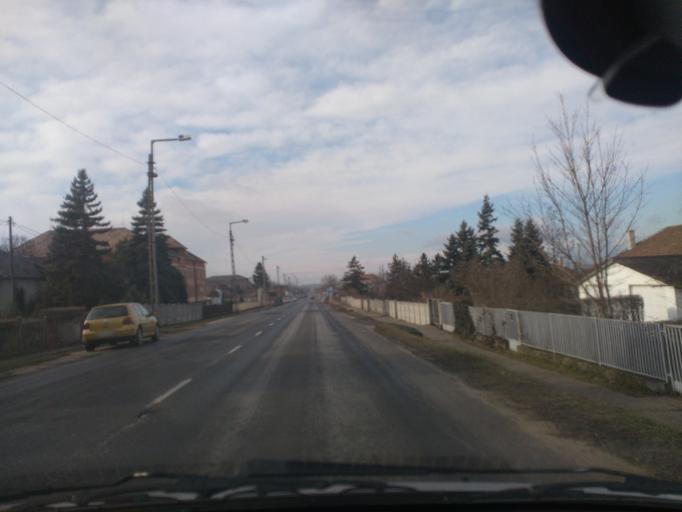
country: HU
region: Komarom-Esztergom
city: Tokod
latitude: 47.7319
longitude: 18.6919
